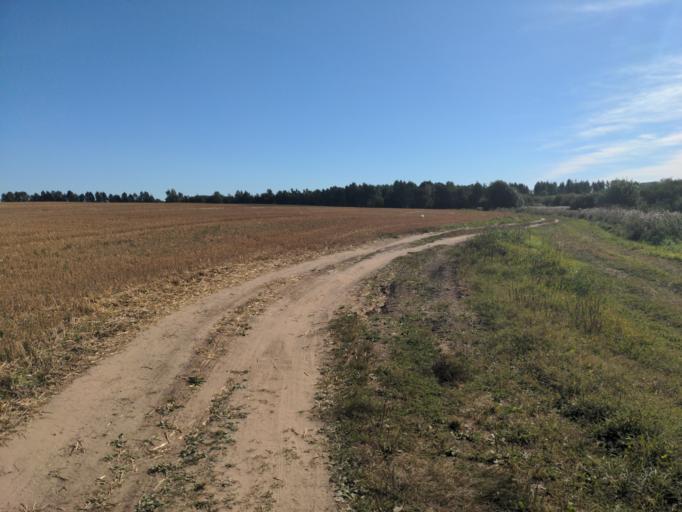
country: LT
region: Siauliu apskritis
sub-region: Siauliai
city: Siauliai
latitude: 55.9263
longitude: 23.2368
